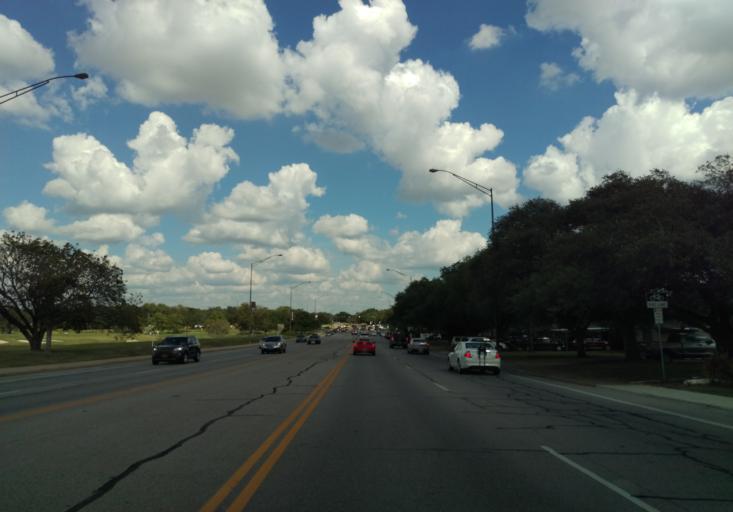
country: US
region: Texas
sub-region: Brazos County
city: College Station
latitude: 30.6164
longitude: -96.3260
